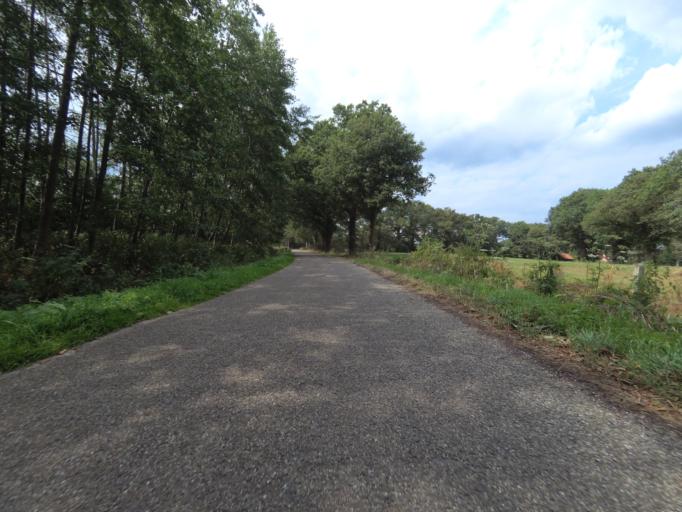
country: NL
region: Overijssel
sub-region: Gemeente Hof van Twente
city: Delden
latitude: 52.2395
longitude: 6.7495
